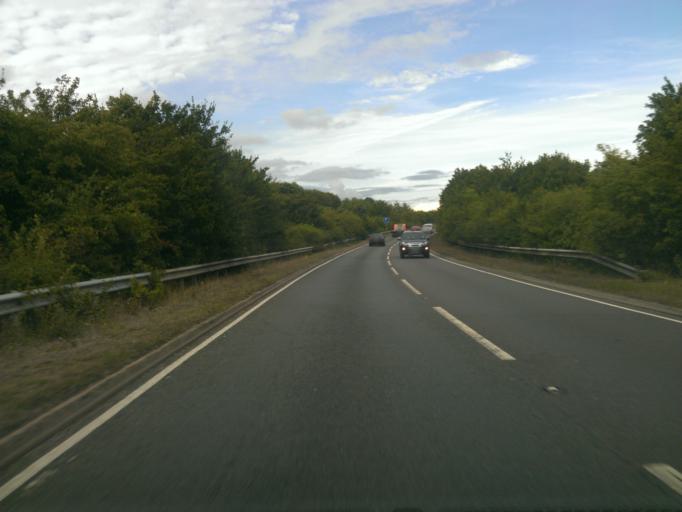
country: GB
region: England
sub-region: Essex
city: Coggeshall
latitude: 51.8808
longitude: 0.6787
